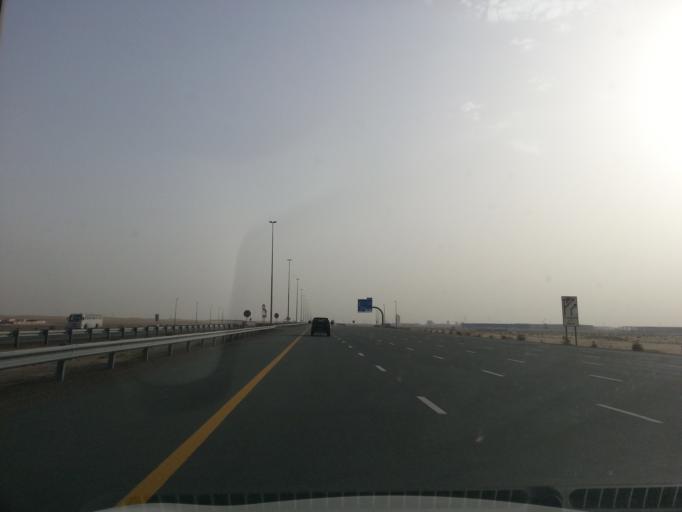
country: AE
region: Dubai
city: Dubai
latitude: 24.8167
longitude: 55.1143
